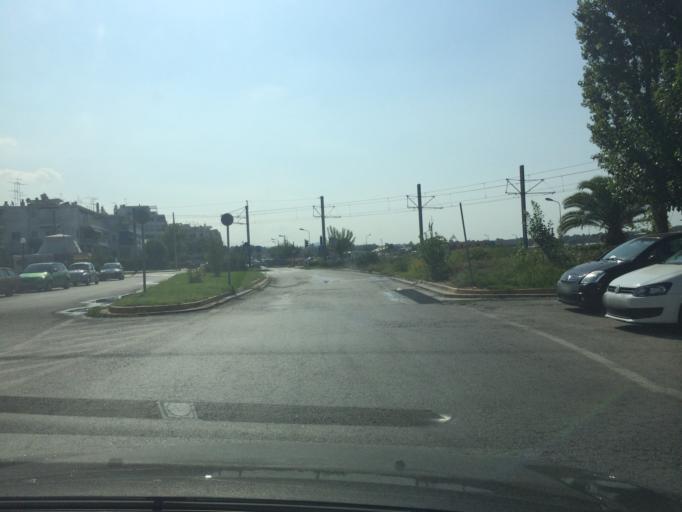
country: GR
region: Attica
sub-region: Nomarchia Athinas
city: Glyfada
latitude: 37.8631
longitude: 23.7455
